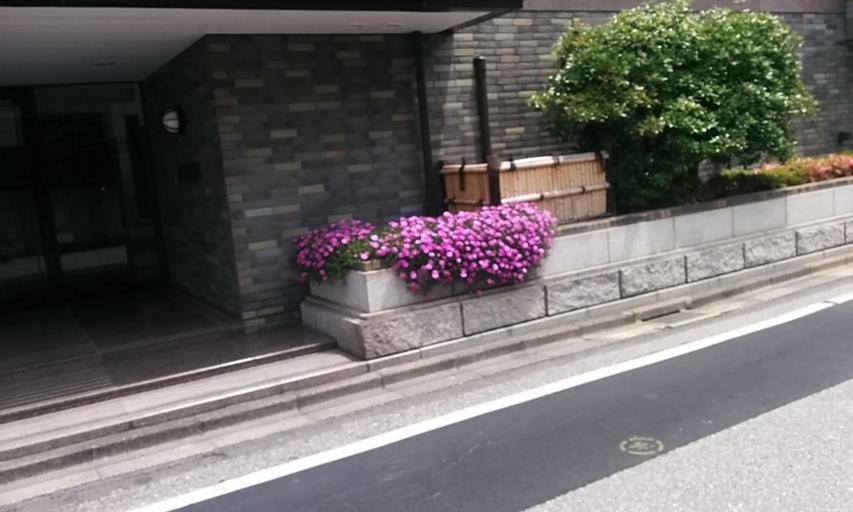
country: JP
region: Tokyo
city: Tokyo
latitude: 35.7201
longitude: 139.7041
